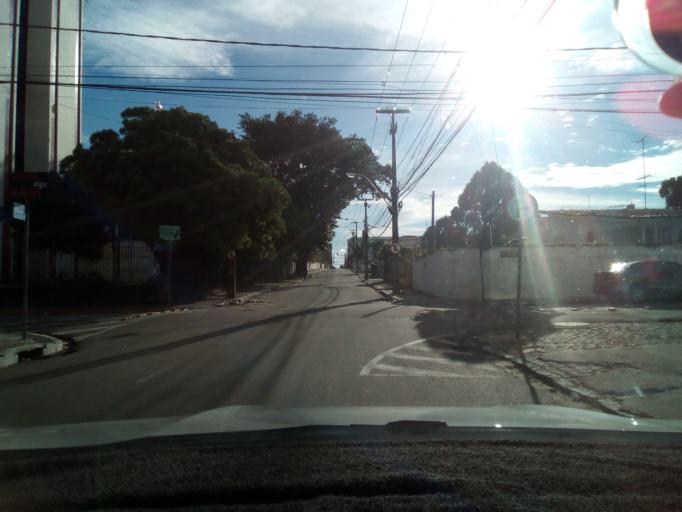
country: BR
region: Paraiba
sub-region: Joao Pessoa
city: Joao Pessoa
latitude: -7.1186
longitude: -34.8570
